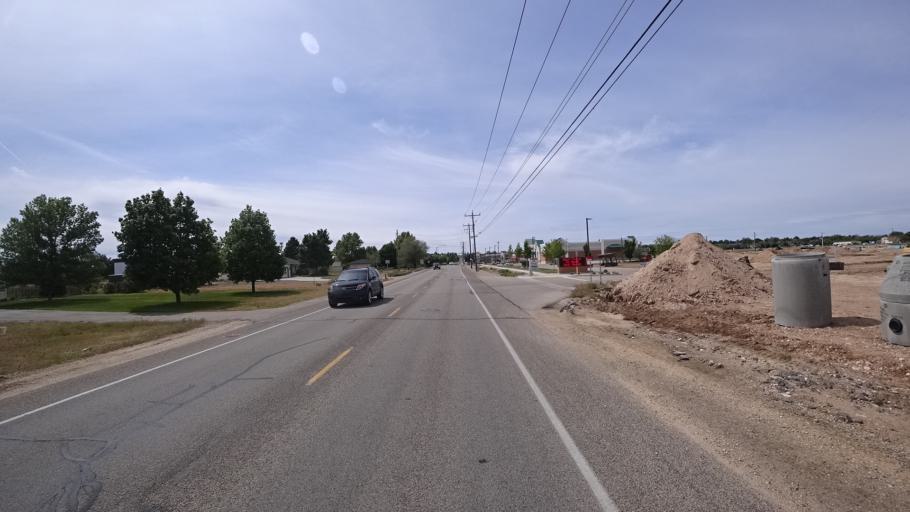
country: US
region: Idaho
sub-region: Ada County
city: Meridian
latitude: 43.5482
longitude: -116.3144
